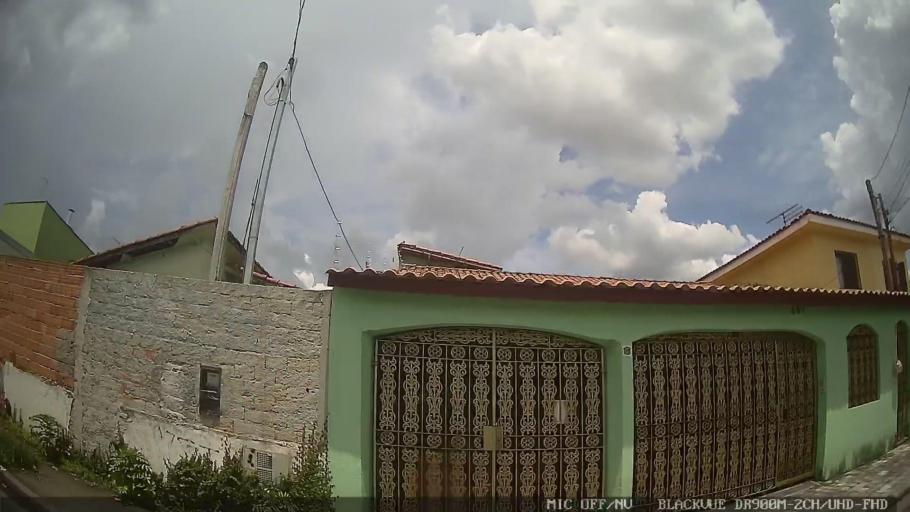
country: BR
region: Sao Paulo
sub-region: Suzano
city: Suzano
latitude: -23.5356
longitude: -46.3170
